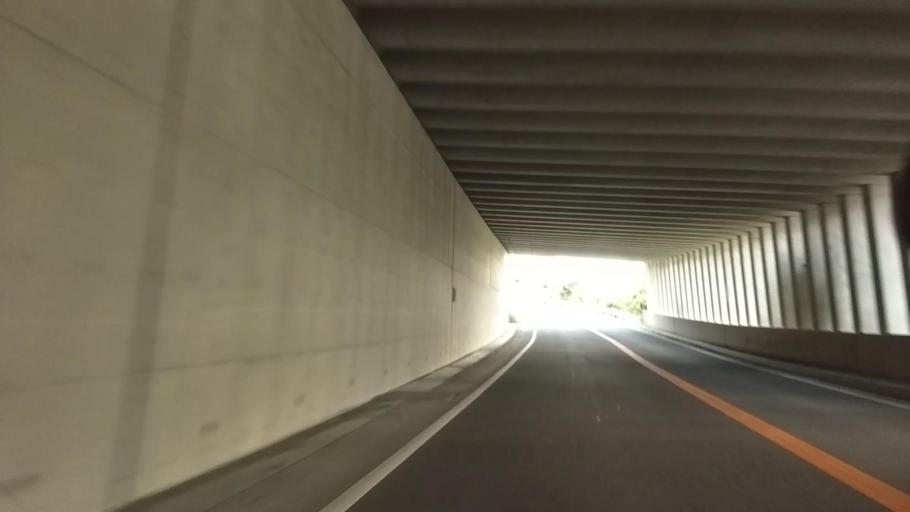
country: JP
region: Shizuoka
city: Fujinomiya
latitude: 35.3950
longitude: 138.4425
